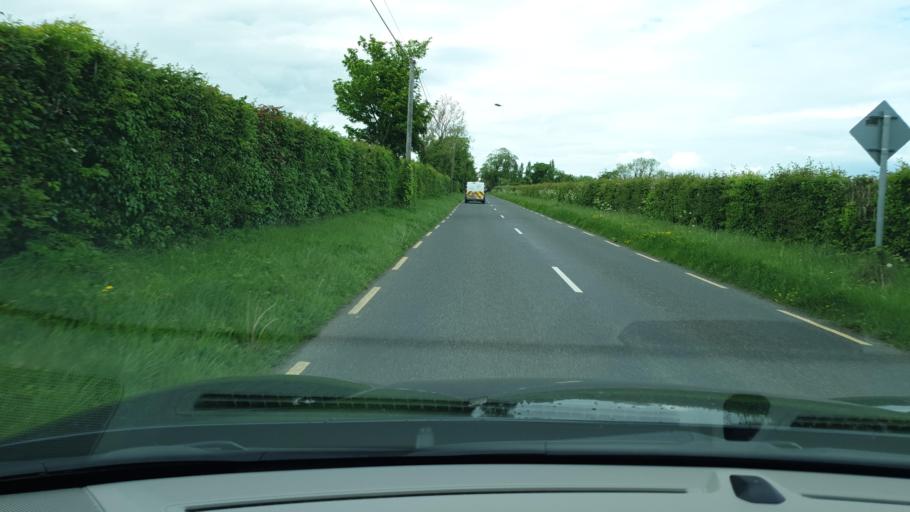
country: IE
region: Leinster
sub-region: An Mhi
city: Ratoath
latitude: 53.4873
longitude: -6.4341
